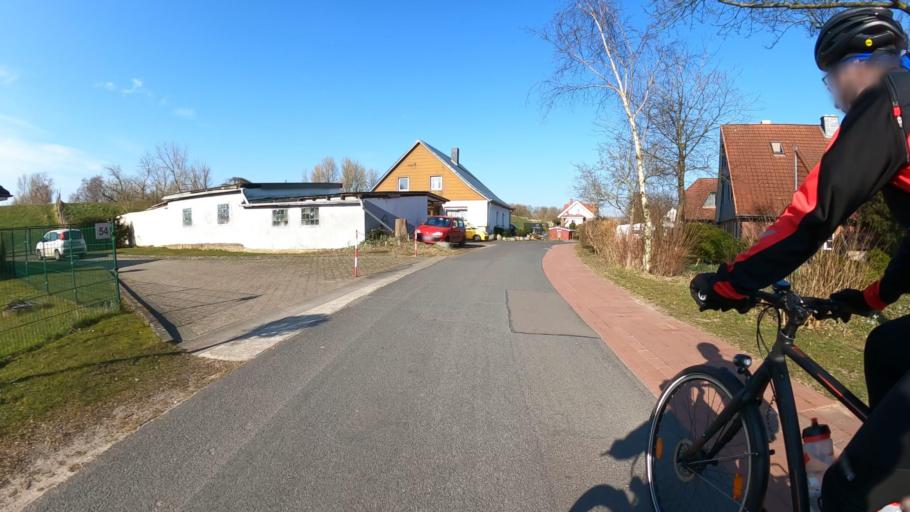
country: DE
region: Schleswig-Holstein
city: Seester
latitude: 53.7217
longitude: 9.5871
